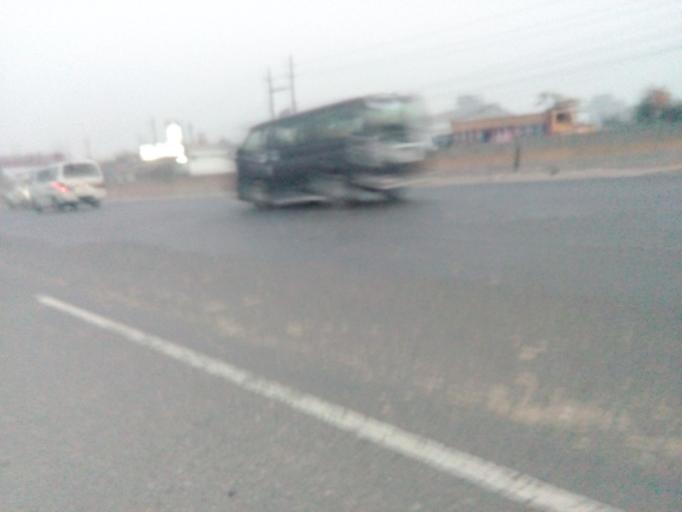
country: BD
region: Dhaka
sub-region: Dhaka
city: Dhaka
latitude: 23.6932
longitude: 90.4740
